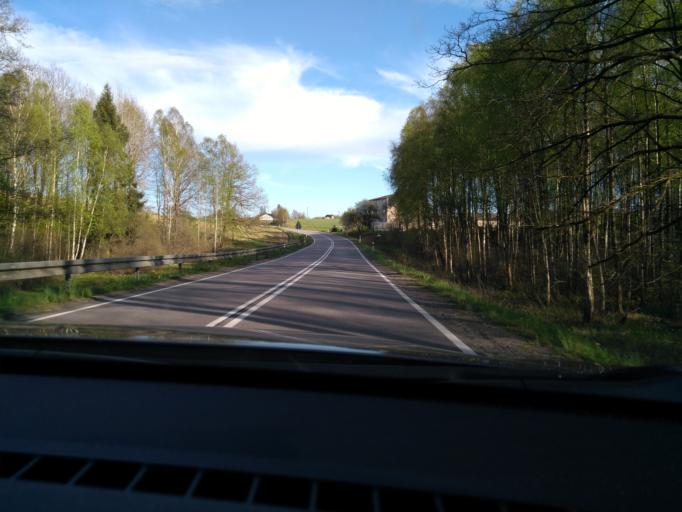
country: PL
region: Pomeranian Voivodeship
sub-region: Powiat leborski
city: Cewice
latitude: 54.3358
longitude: 17.7092
